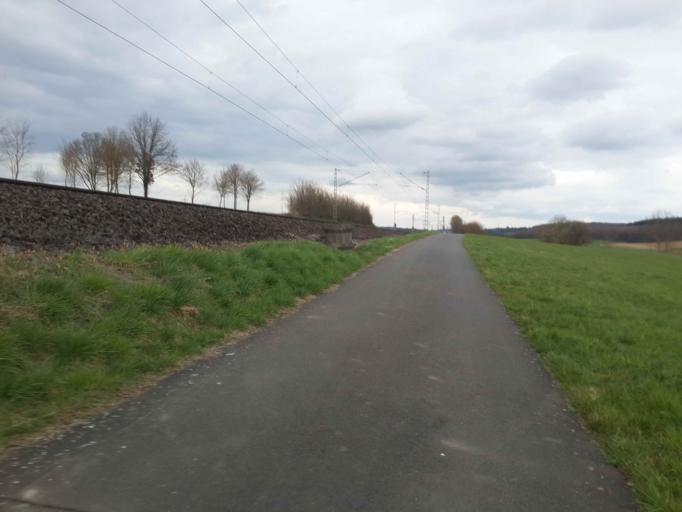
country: DE
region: Baden-Wuerttemberg
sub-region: Karlsruhe Region
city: Rosenberg
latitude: 49.4768
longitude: 9.5077
